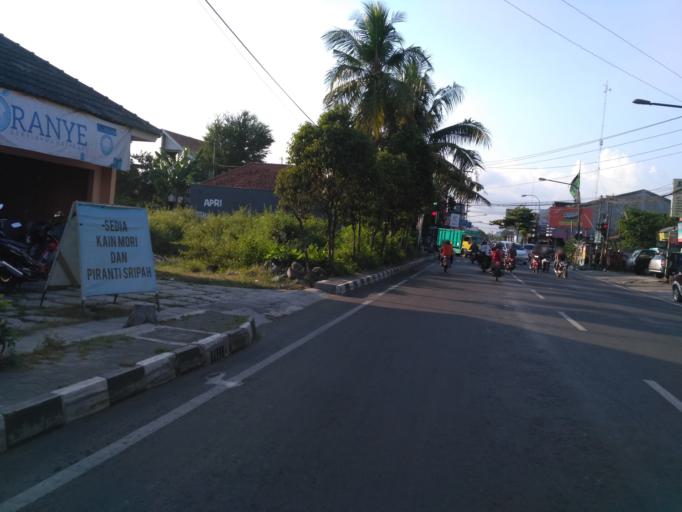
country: ID
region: Daerah Istimewa Yogyakarta
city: Yogyakarta
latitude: -7.8265
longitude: 110.3901
